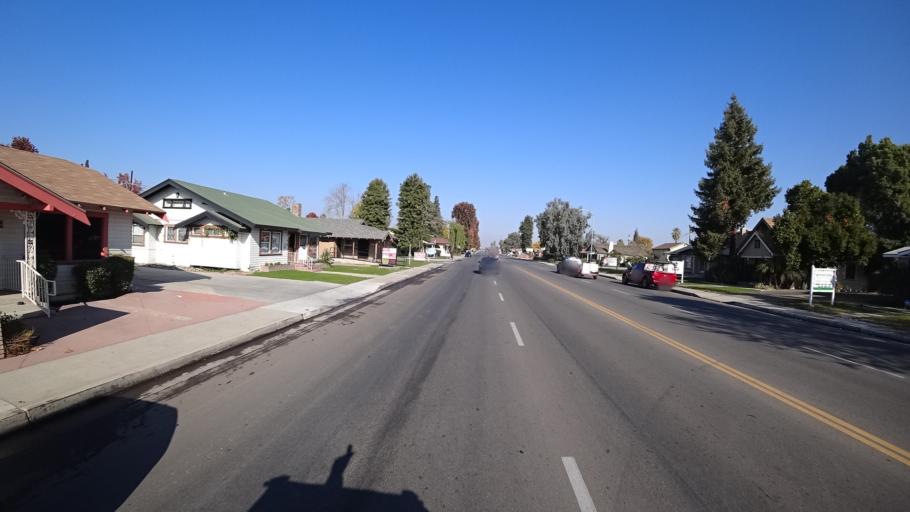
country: US
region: California
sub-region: Kern County
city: Bakersfield
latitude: 35.3565
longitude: -119.0214
